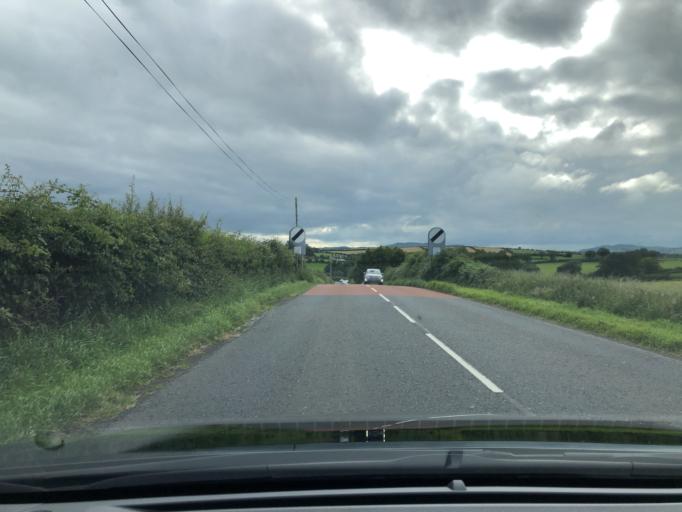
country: GB
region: Northern Ireland
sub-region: Down District
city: Dundrum
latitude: 54.2886
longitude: -5.8413
